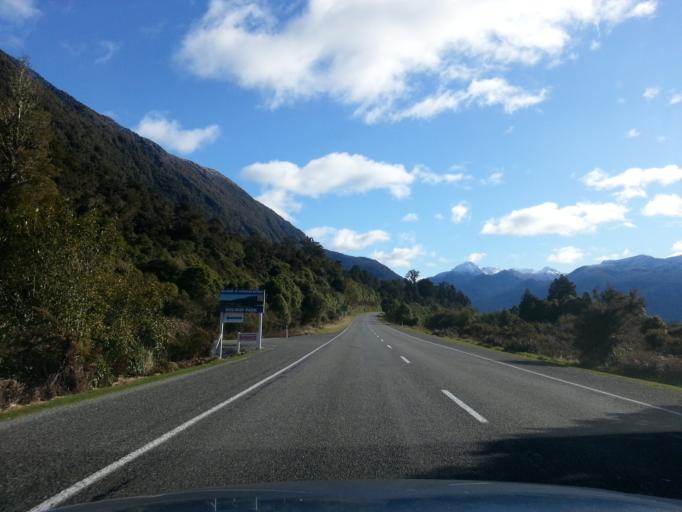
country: NZ
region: West Coast
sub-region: Grey District
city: Greymouth
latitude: -42.7438
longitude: 171.5099
